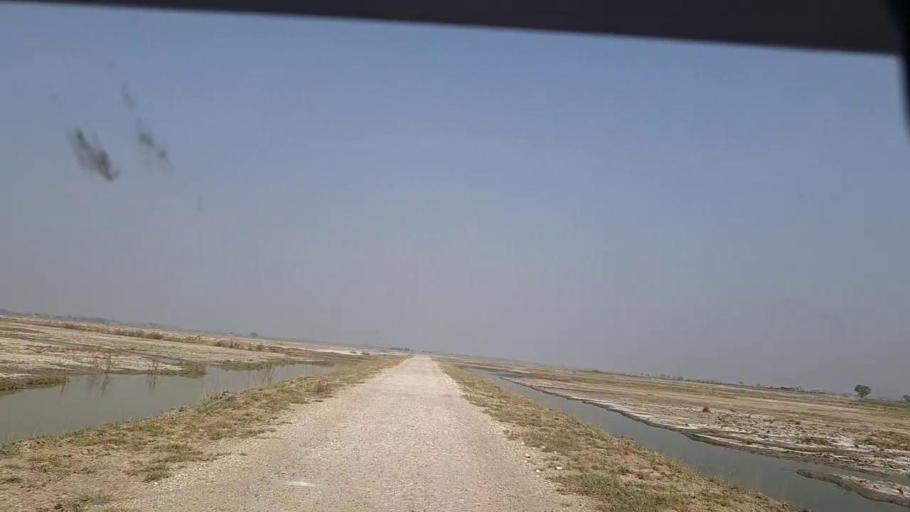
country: PK
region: Sindh
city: Shikarpur
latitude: 28.0462
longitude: 68.6530
